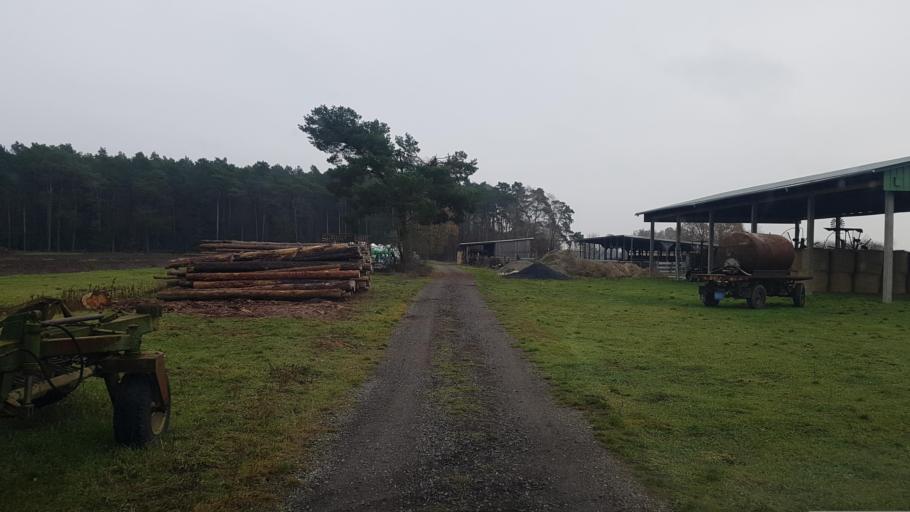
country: DE
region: Brandenburg
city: Sallgast
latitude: 51.6471
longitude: 13.8424
